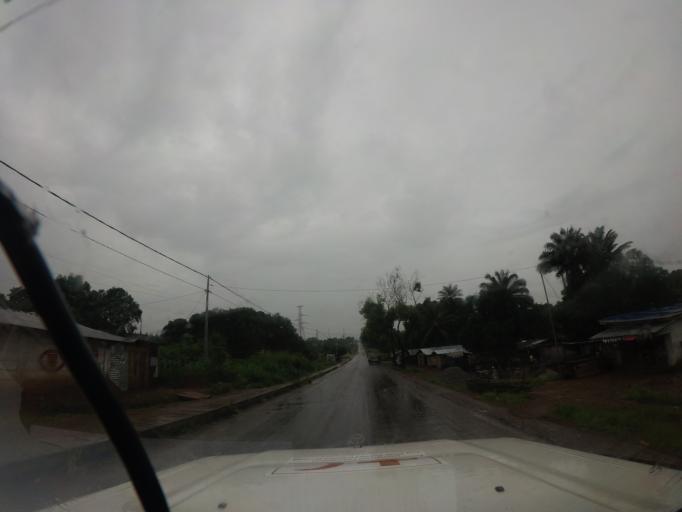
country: SL
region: Northern Province
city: Makeni
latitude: 8.9017
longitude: -12.0356
